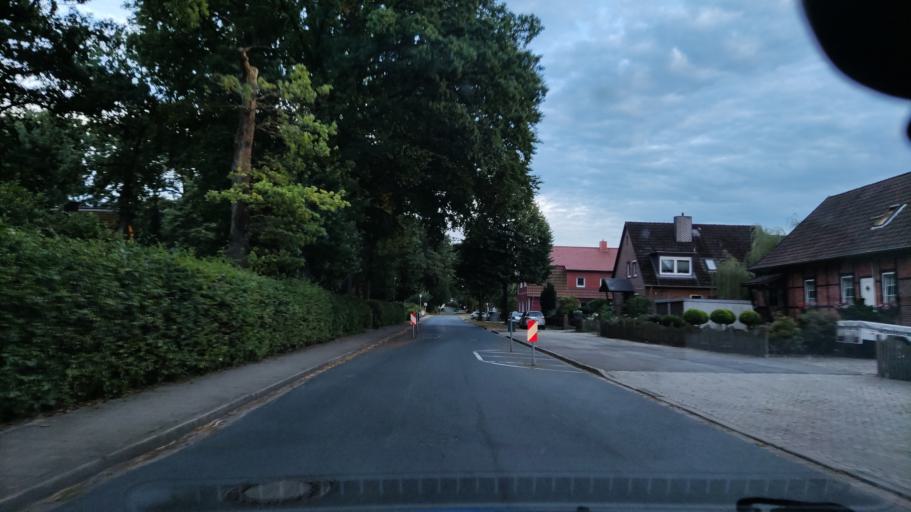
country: DE
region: Lower Saxony
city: Soltau
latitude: 52.9888
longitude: 9.9055
